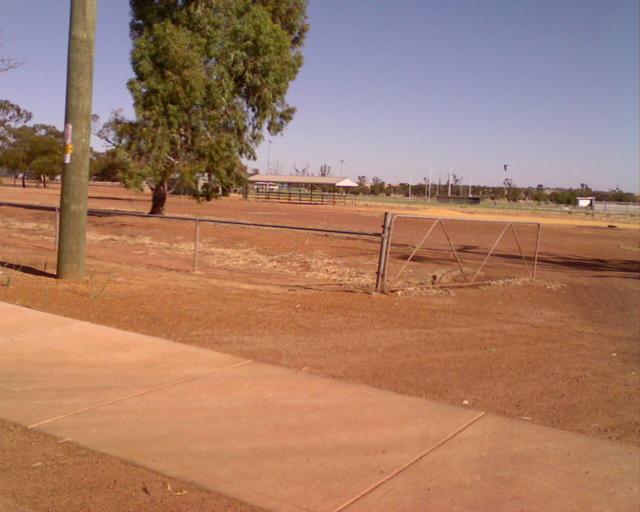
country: AU
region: Western Australia
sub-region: Wongan-Ballidu
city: Wongan Hills
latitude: -30.2764
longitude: 116.6582
